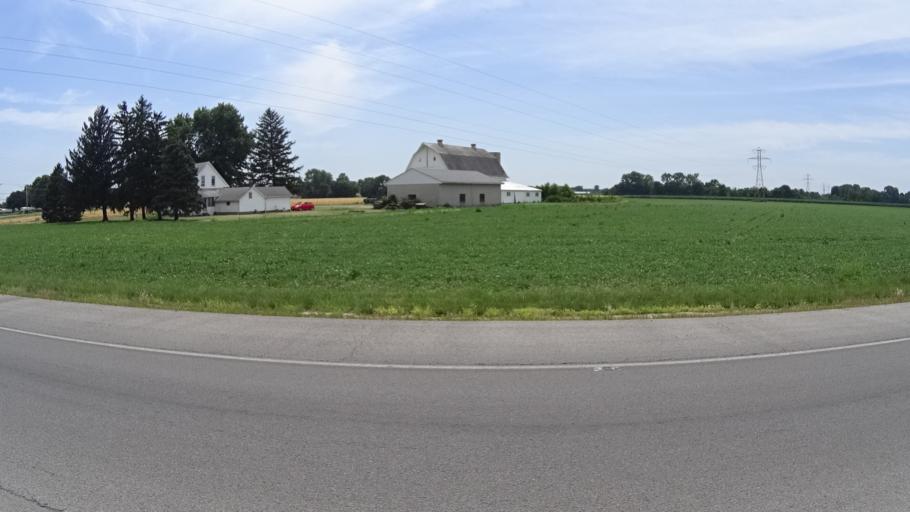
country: US
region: Ohio
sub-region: Erie County
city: Sandusky
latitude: 41.4331
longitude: -82.7438
